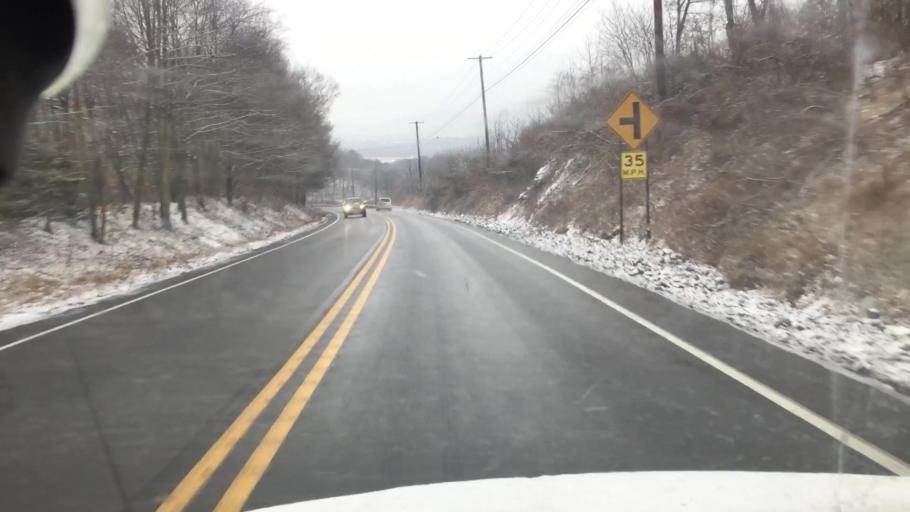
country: US
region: Pennsylvania
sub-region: Luzerne County
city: Nescopeck
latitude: 41.0529
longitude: -76.1676
